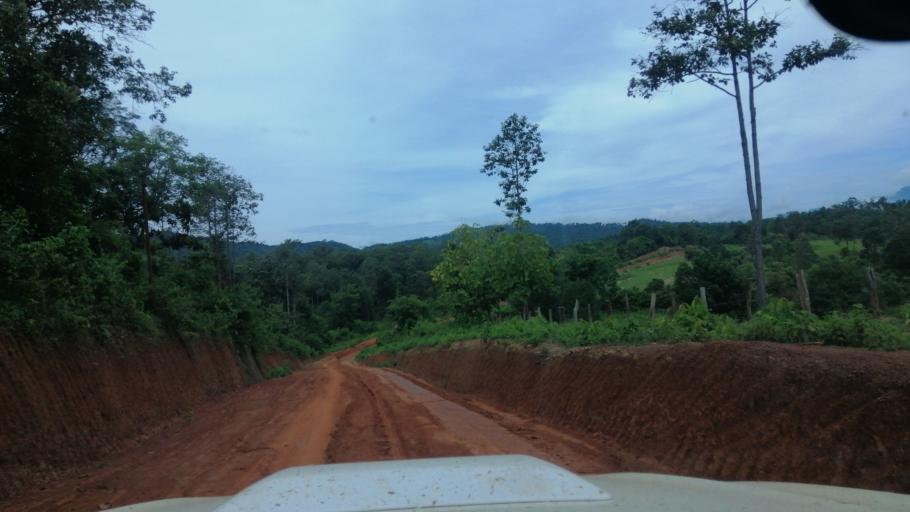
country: TH
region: Loei
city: Na Haeo
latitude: 17.5782
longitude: 101.1553
